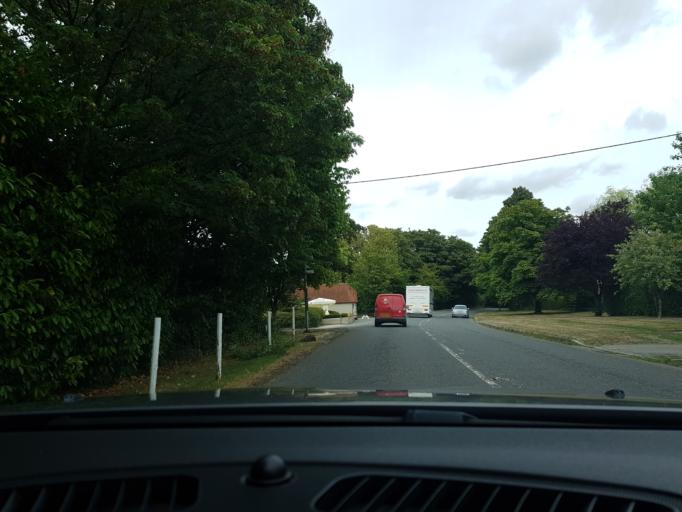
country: GB
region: England
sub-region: Hampshire
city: Highclere
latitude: 51.3334
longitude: -1.3444
